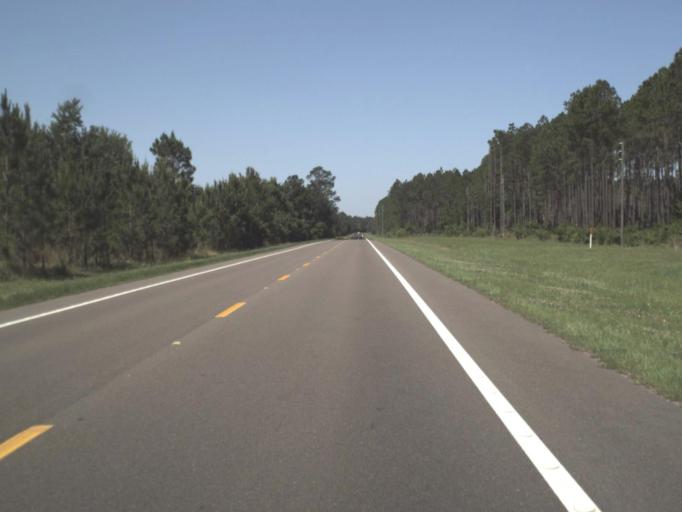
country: US
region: Florida
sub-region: Duval County
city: Baldwin
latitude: 30.2979
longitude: -82.0368
